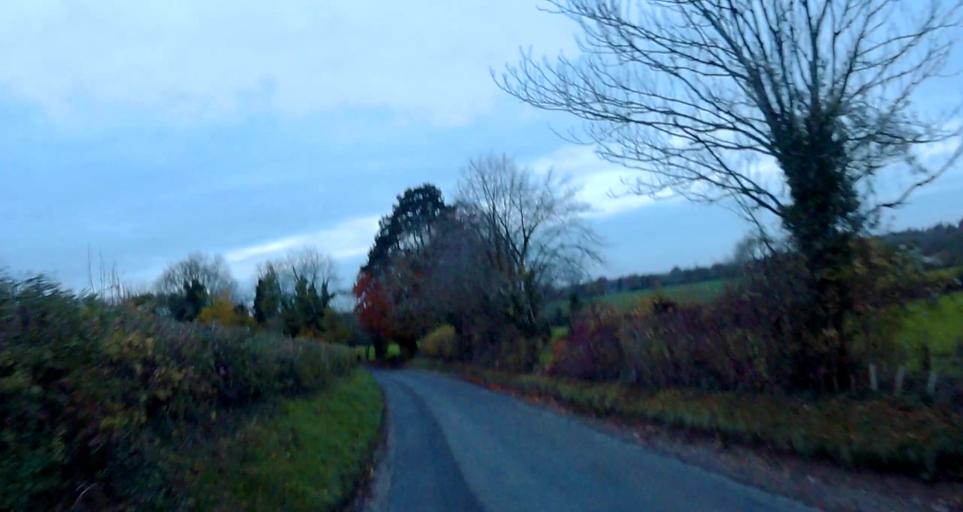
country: GB
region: England
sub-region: Hampshire
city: Old Basing
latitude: 51.2336
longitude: -1.0173
